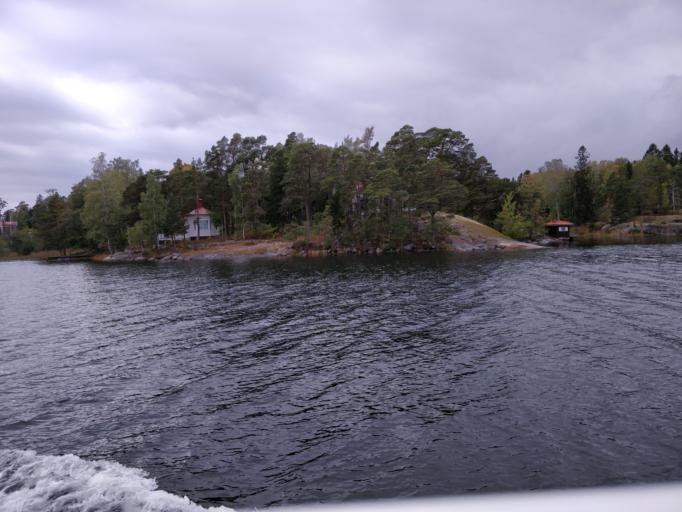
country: FI
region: Uusimaa
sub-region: Helsinki
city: Vantaa
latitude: 60.1616
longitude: 25.0995
